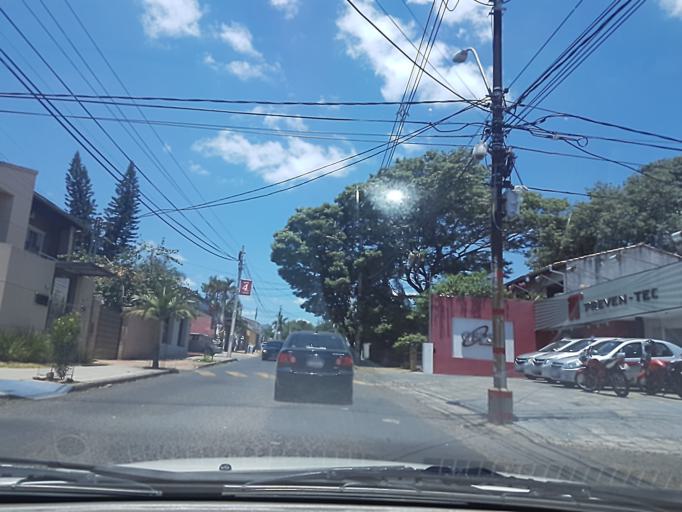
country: PY
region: Asuncion
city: Asuncion
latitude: -25.2957
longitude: -57.5900
